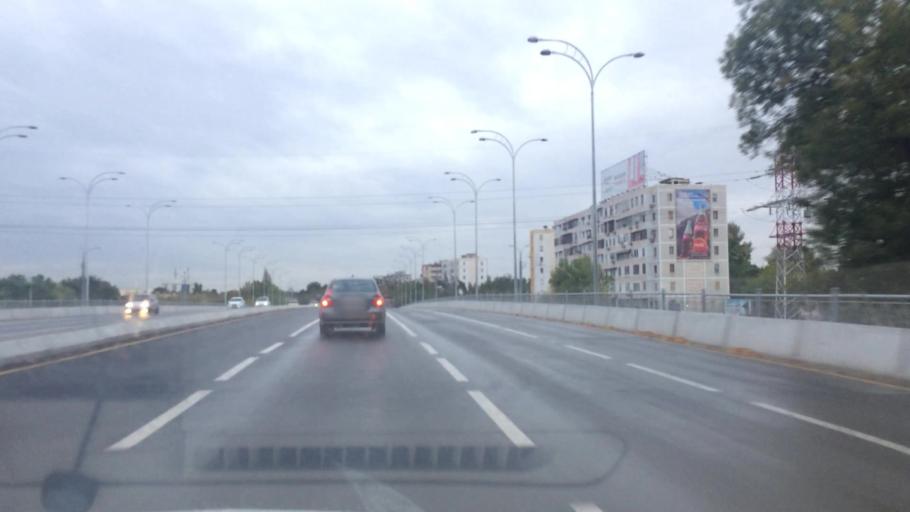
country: UZ
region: Toshkent Shahri
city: Tashkent
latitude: 41.2755
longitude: 69.2055
